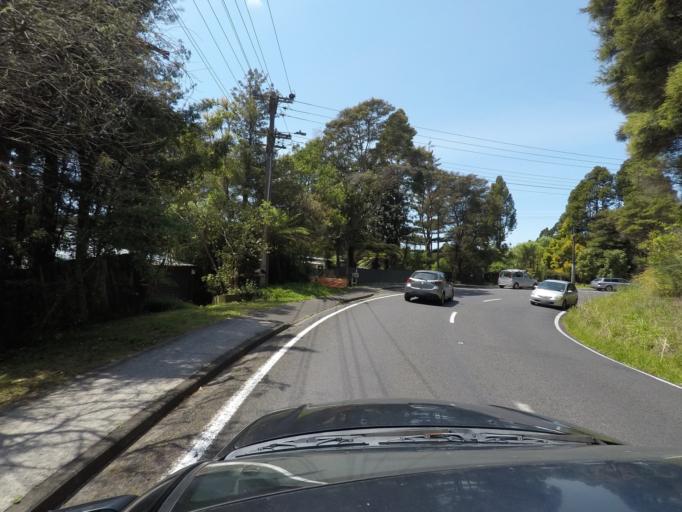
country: NZ
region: Auckland
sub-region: Auckland
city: Titirangi
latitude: -36.9576
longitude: 174.6383
